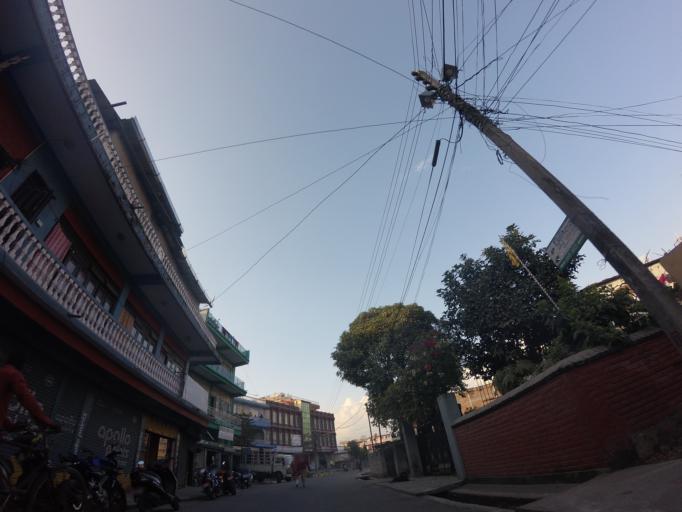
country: NP
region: Western Region
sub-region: Gandaki Zone
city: Pokhara
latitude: 28.2056
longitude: 83.9996
